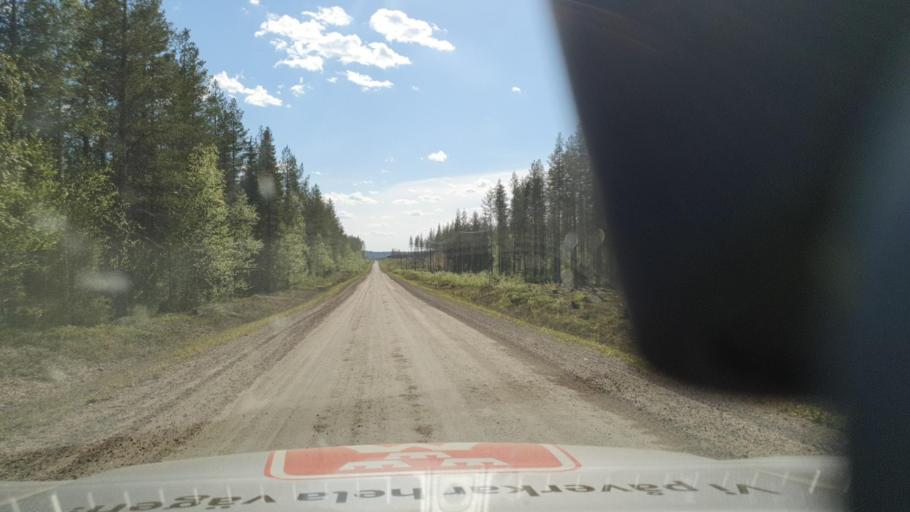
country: SE
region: Norrbotten
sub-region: Bodens Kommun
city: Boden
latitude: 66.5468
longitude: 21.9545
